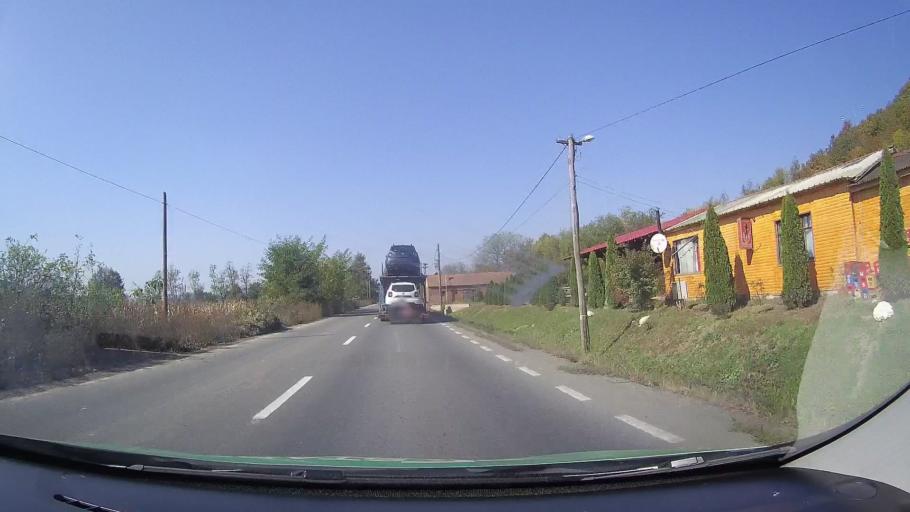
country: RO
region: Arad
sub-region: Comuna Barzava
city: Barzava
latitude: 46.1002
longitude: 22.0125
